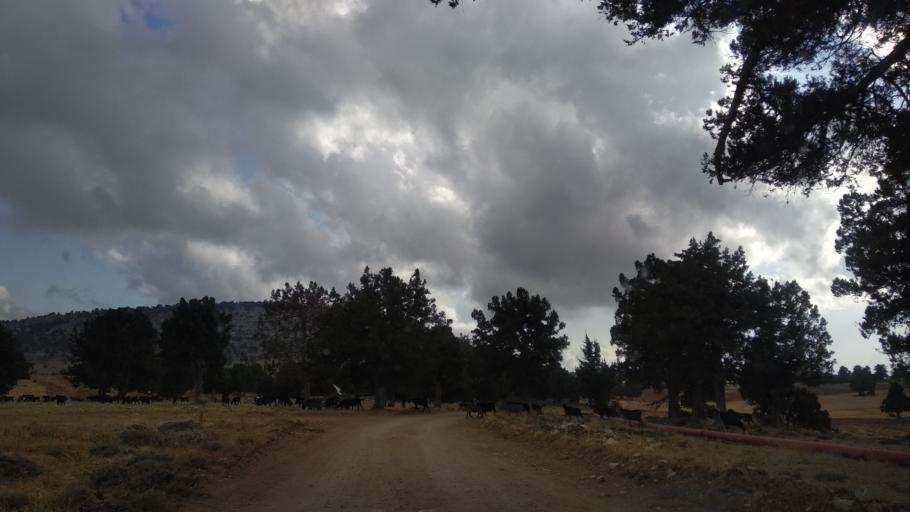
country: TR
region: Mersin
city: Sarikavak
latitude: 36.5664
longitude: 33.7400
